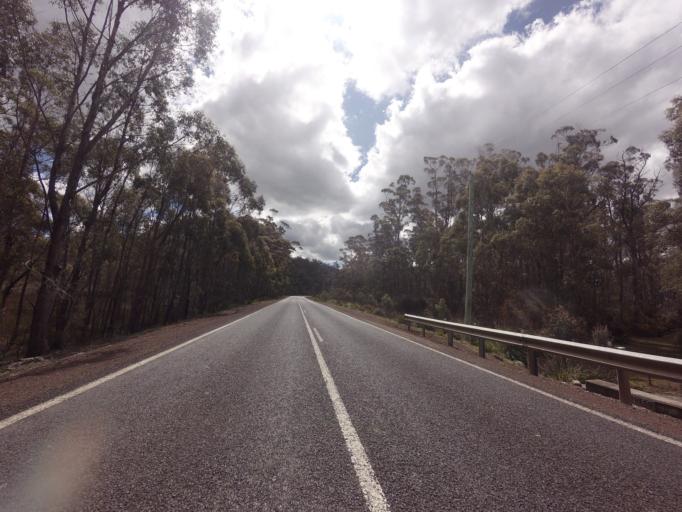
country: AU
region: Tasmania
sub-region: Northern Midlands
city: Evandale
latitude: -42.0173
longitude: 147.7372
